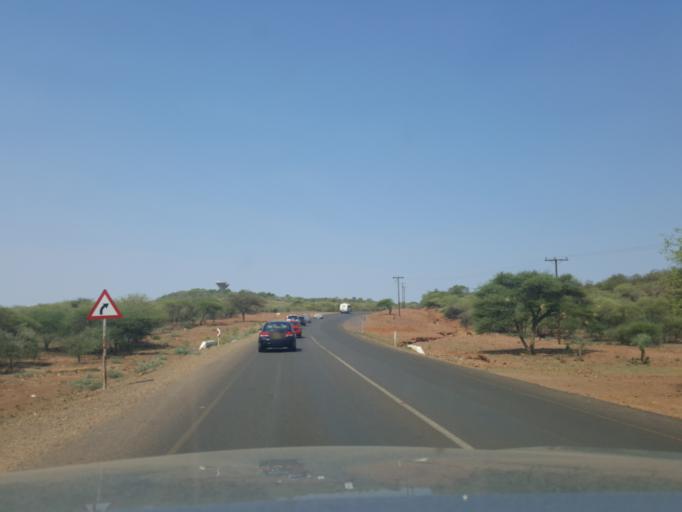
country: BW
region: South East
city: Ramotswa
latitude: -24.8599
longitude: 25.8408
